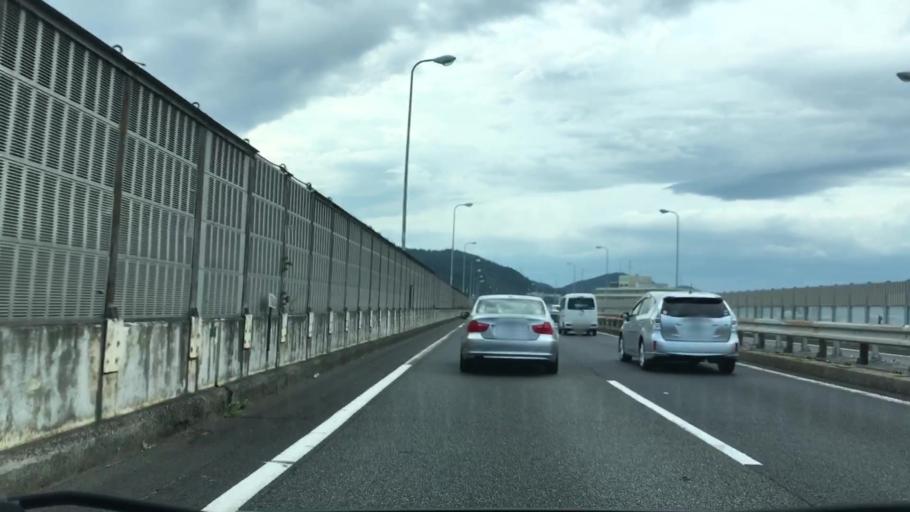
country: JP
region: Hyogo
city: Kakogawacho-honmachi
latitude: 34.7869
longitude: 134.7765
